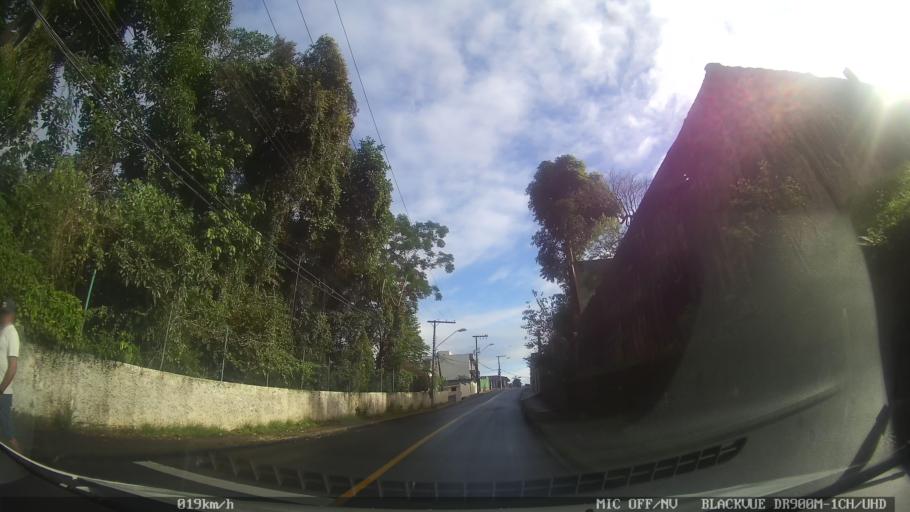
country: BR
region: Santa Catarina
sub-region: Sao Jose
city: Campinas
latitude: -27.6152
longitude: -48.6293
